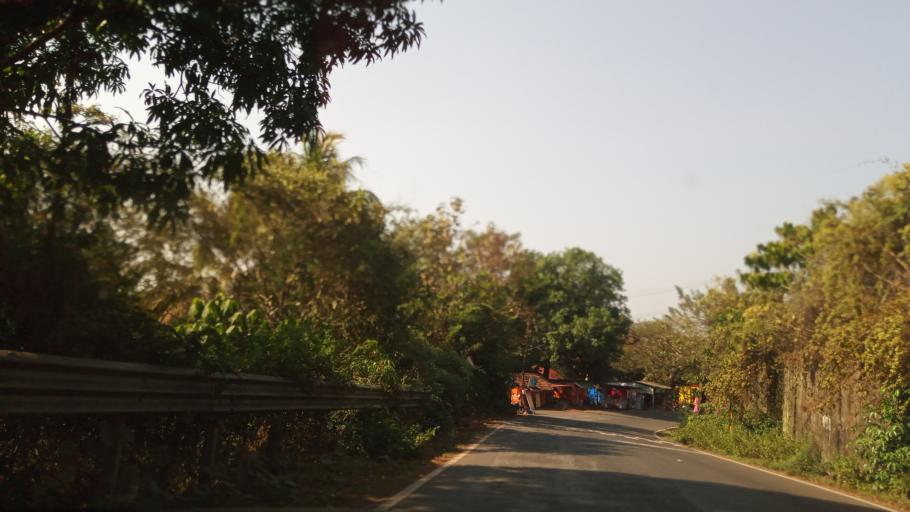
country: IN
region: Goa
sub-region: North Goa
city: Bandora
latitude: 15.4611
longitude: 73.9601
